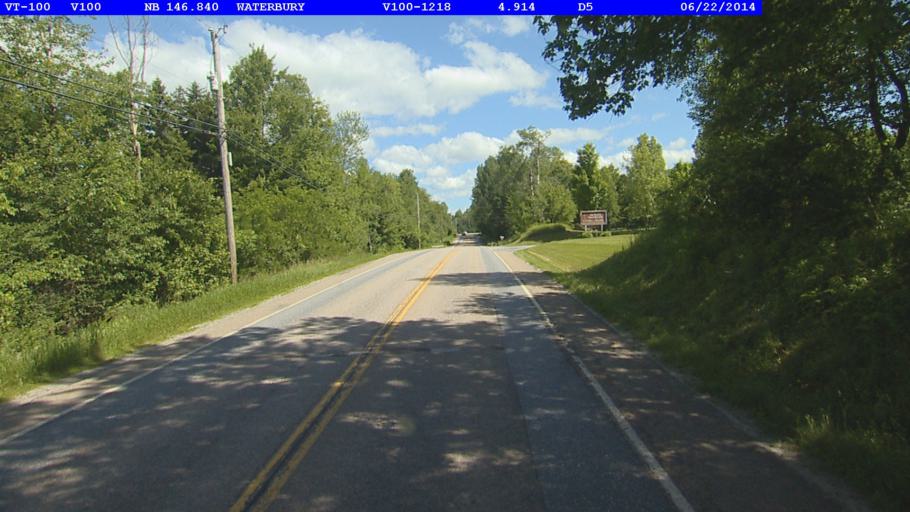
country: US
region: Vermont
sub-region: Washington County
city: Waterbury
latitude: 44.3999
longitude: -72.7190
